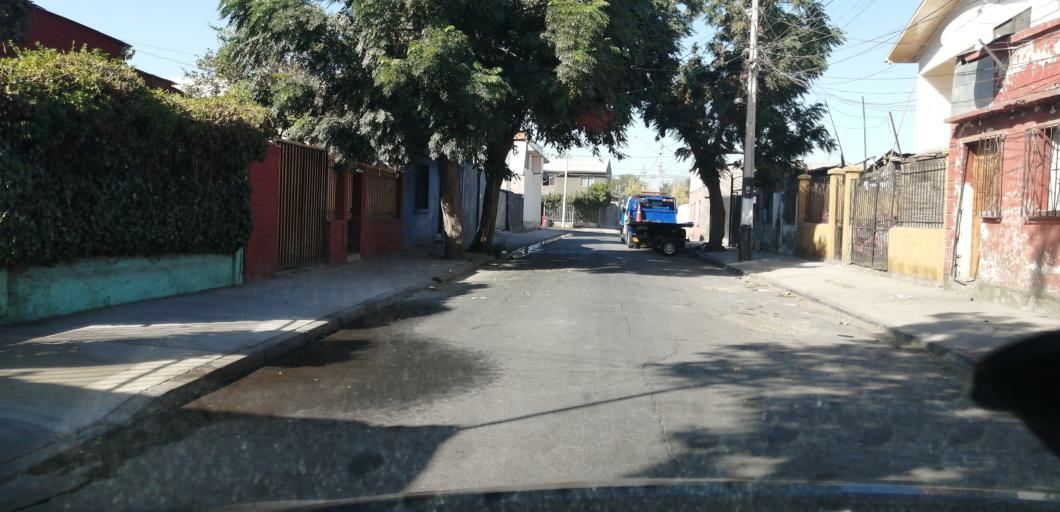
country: CL
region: Santiago Metropolitan
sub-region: Provincia de Santiago
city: Lo Prado
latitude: -33.4297
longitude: -70.7676
